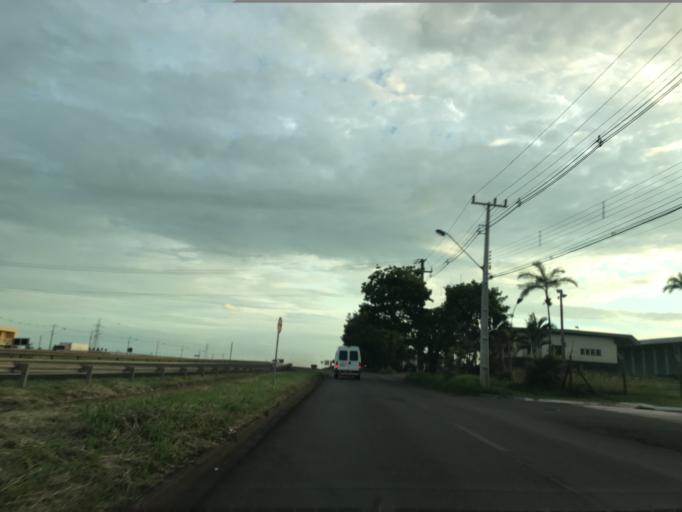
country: BR
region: Parana
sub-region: Maringa
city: Maringa
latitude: -23.4084
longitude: -51.9860
